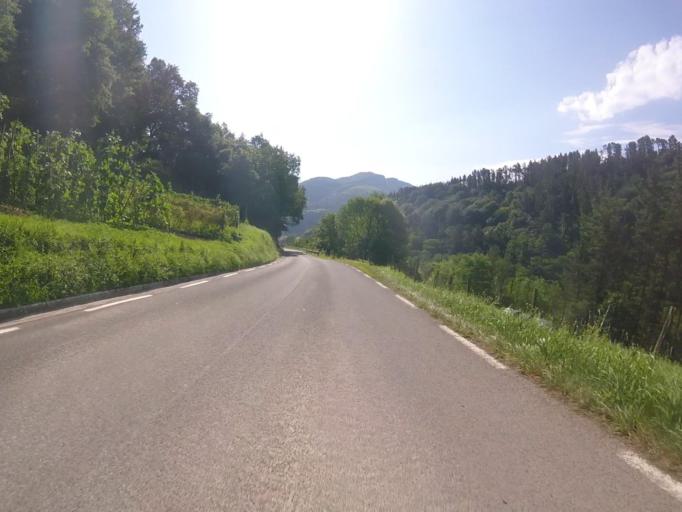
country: ES
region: Basque Country
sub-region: Provincia de Guipuzcoa
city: Hernialde
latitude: 43.1635
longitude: -2.0829
